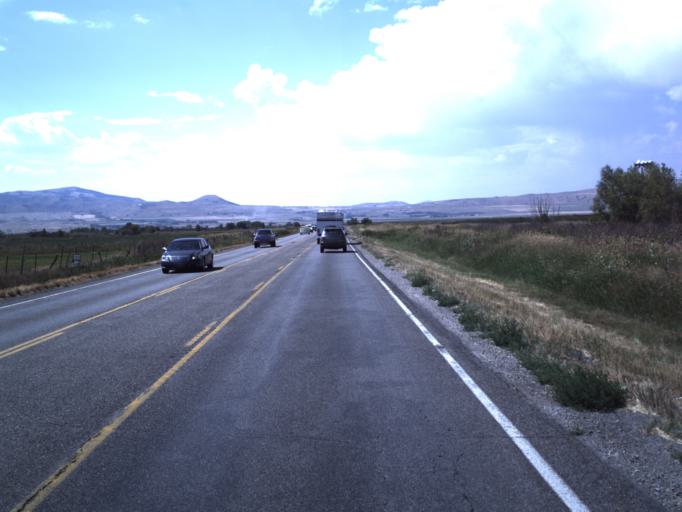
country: US
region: Utah
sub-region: Cache County
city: Benson
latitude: 41.7401
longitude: -111.9053
